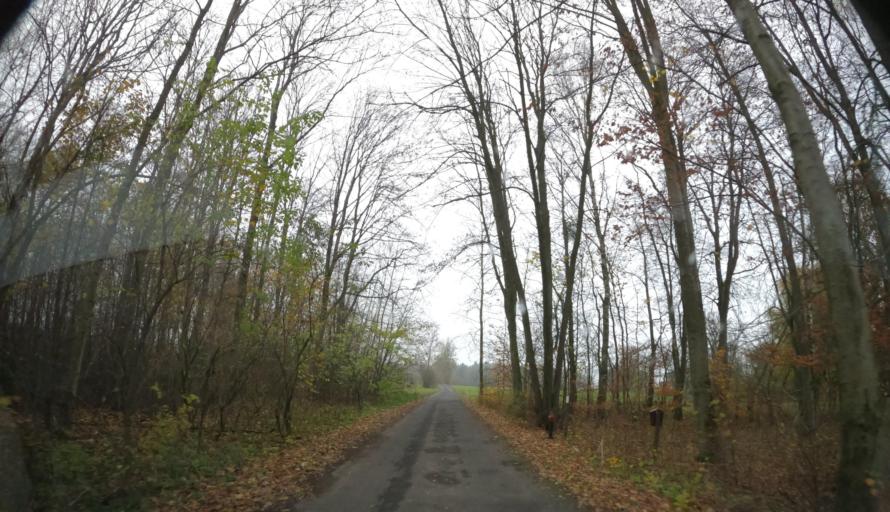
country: PL
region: West Pomeranian Voivodeship
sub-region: Powiat lobeski
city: Radowo Male
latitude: 53.6751
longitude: 15.4513
